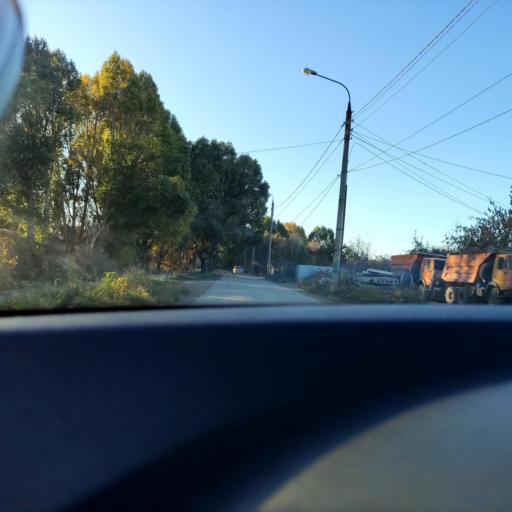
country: RU
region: Samara
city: Smyshlyayevka
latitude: 53.1891
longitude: 50.2840
